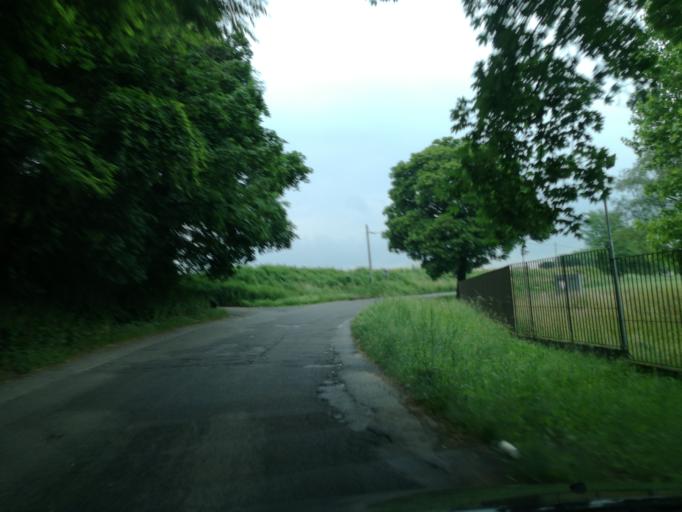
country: IT
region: Lombardy
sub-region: Provincia di Monza e Brianza
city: Concorezzo
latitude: 45.6067
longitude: 9.3470
